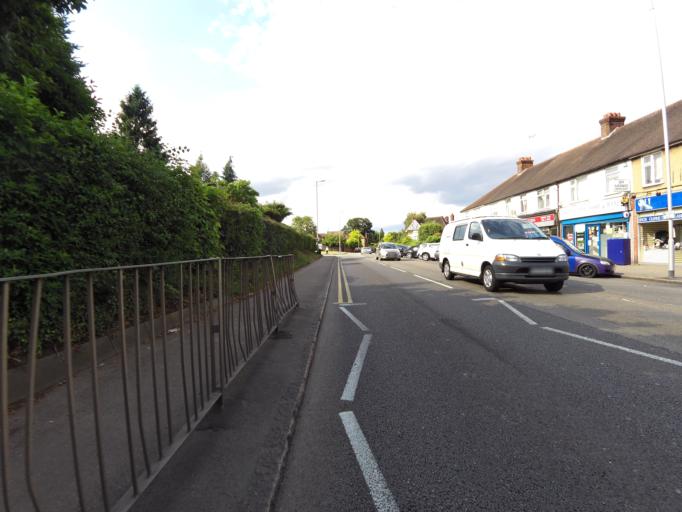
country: GB
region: England
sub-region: Hertfordshire
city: Broxbourne
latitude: 51.7488
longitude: -0.0188
